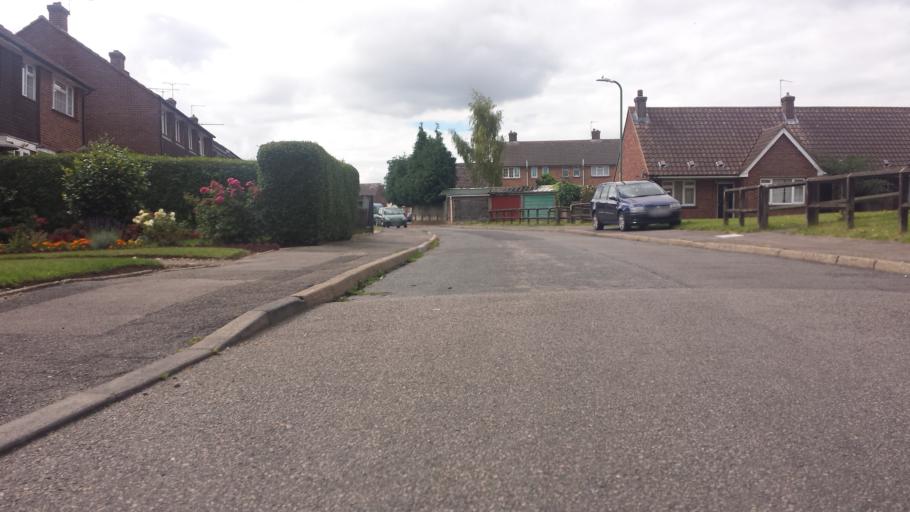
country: GB
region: England
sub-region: Kent
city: Swanley
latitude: 51.4007
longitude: 0.1654
